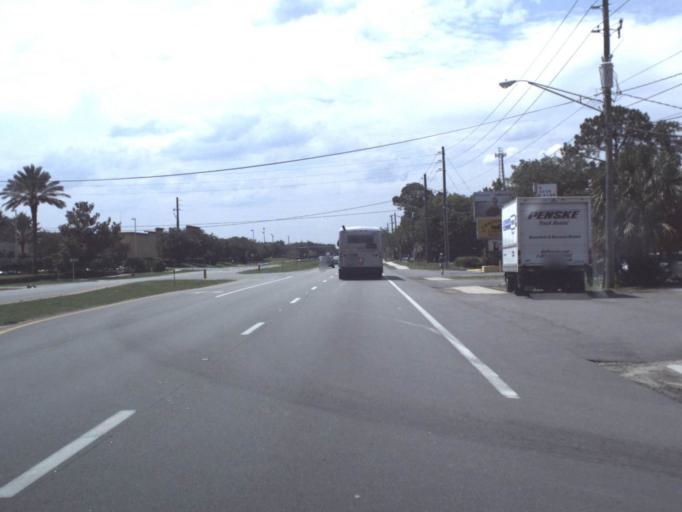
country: US
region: Florida
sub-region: Duval County
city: Jacksonville
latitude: 30.2778
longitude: -81.6264
